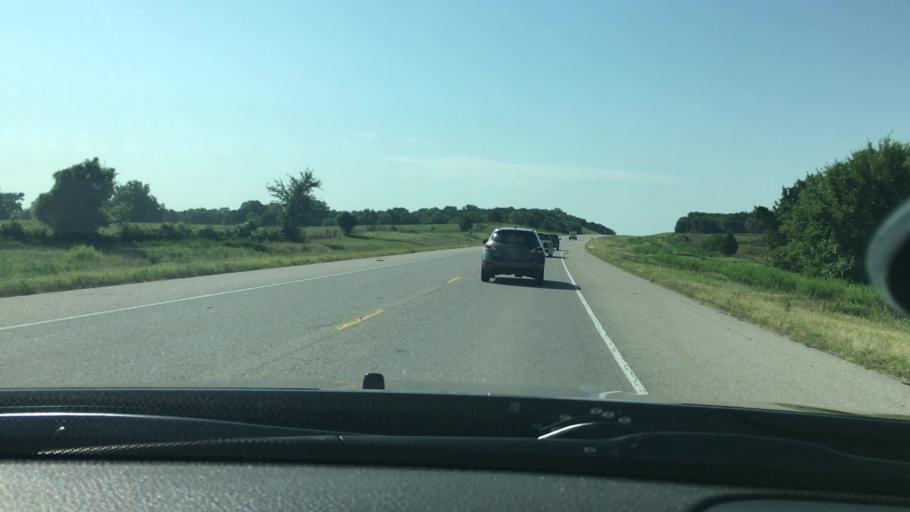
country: US
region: Oklahoma
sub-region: Pontotoc County
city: Ada
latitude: 34.6735
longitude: -96.5721
